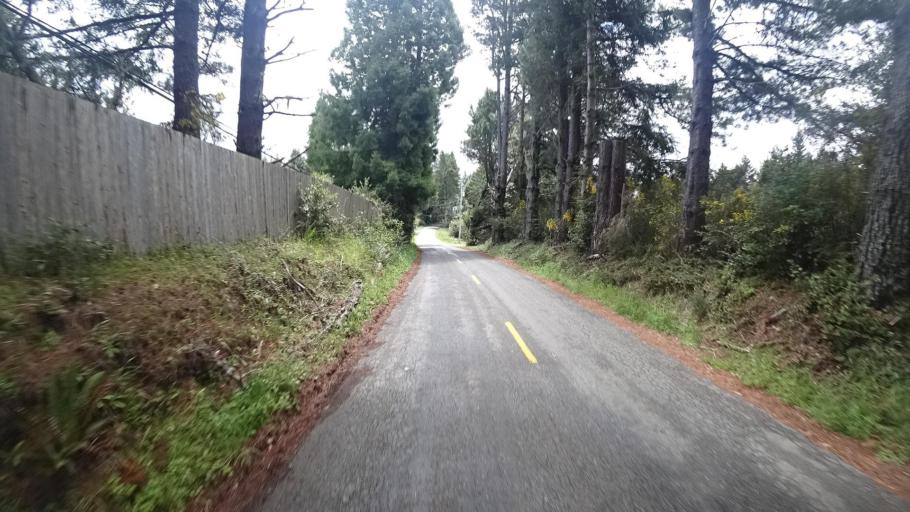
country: US
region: California
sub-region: Humboldt County
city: Bayside
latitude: 40.7693
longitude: -123.9996
